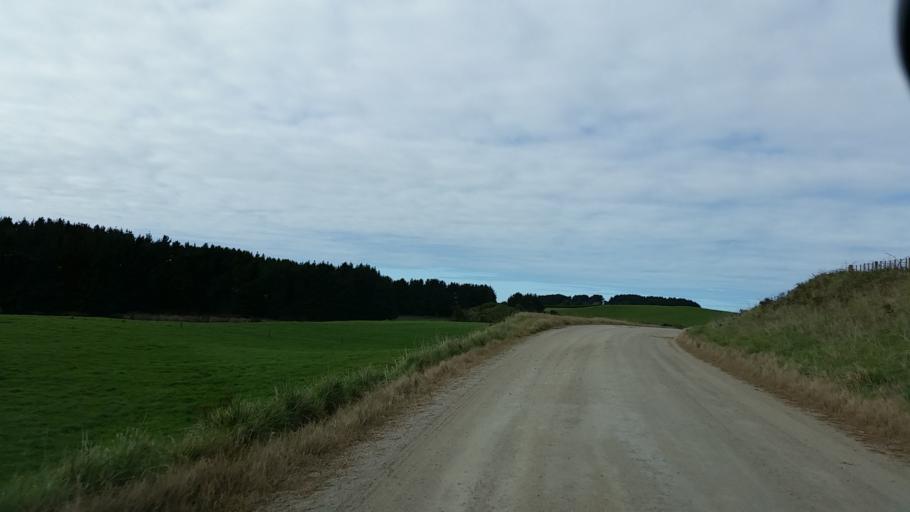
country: NZ
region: Taranaki
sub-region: South Taranaki District
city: Patea
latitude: -39.7983
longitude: 174.6784
